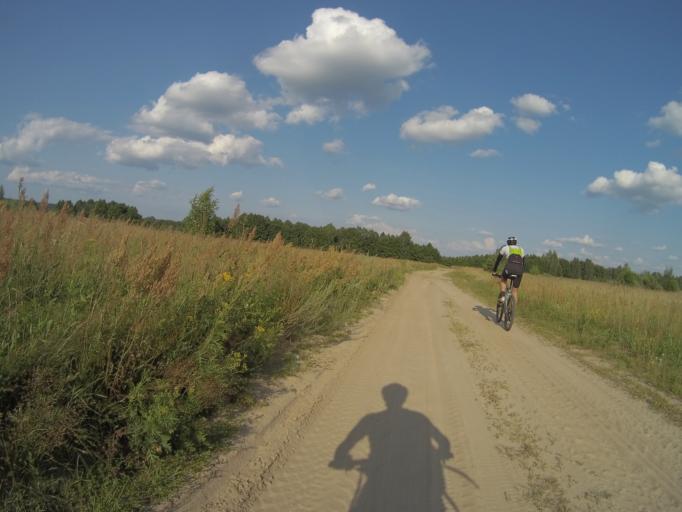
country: RU
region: Vladimir
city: Orgtrud
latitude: 56.1509
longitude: 40.6078
